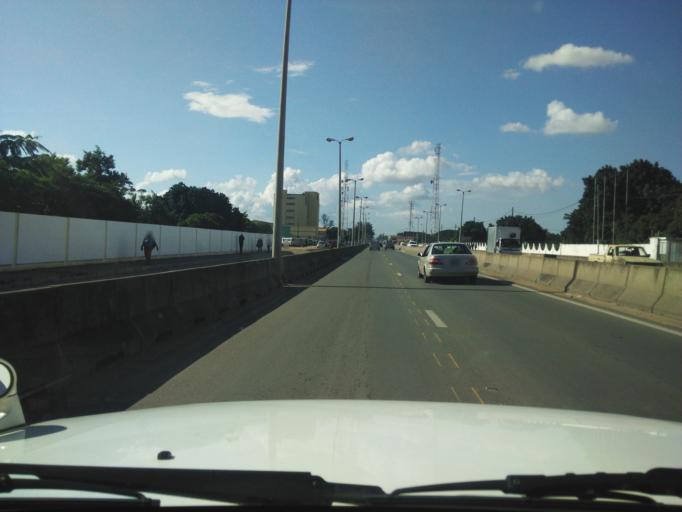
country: MZ
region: Maputo City
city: Maputo
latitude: -25.9385
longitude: 32.5467
